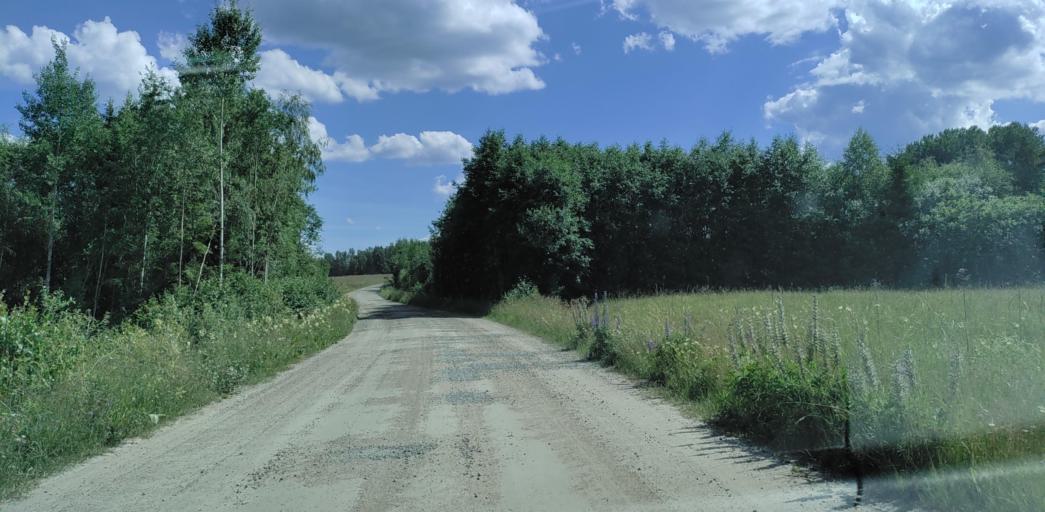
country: SE
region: Vaermland
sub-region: Hagfors Kommun
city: Ekshaerad
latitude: 60.1252
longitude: 13.4785
